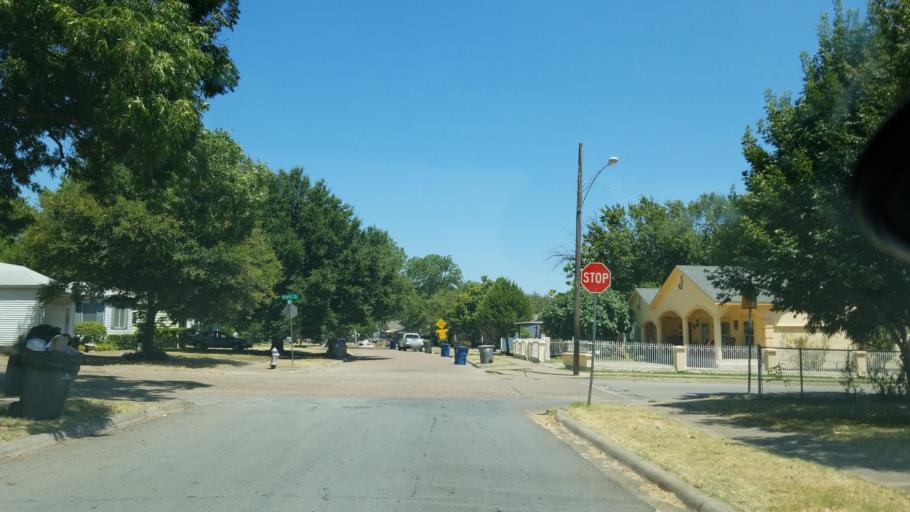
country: US
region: Texas
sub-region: Dallas County
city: Cockrell Hill
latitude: 32.7244
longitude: -96.8823
